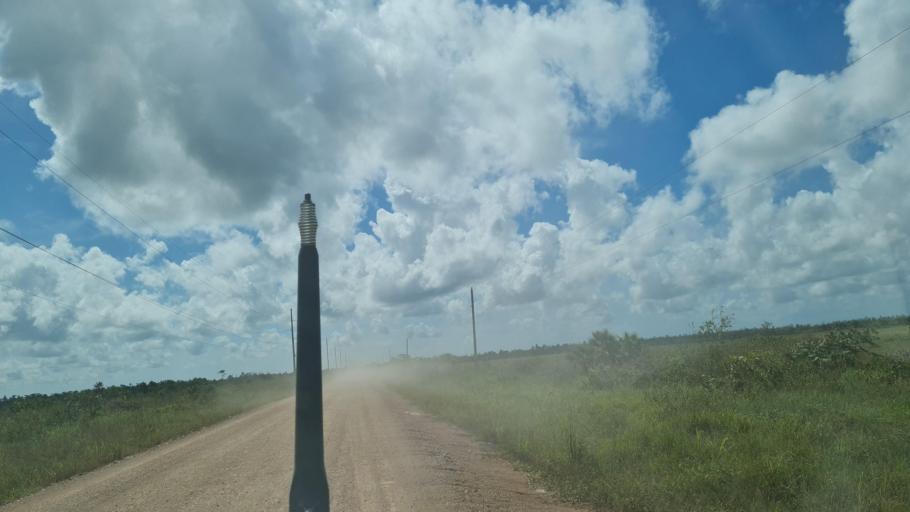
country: NI
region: Atlantico Norte (RAAN)
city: Puerto Cabezas
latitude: 14.1094
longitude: -83.5893
